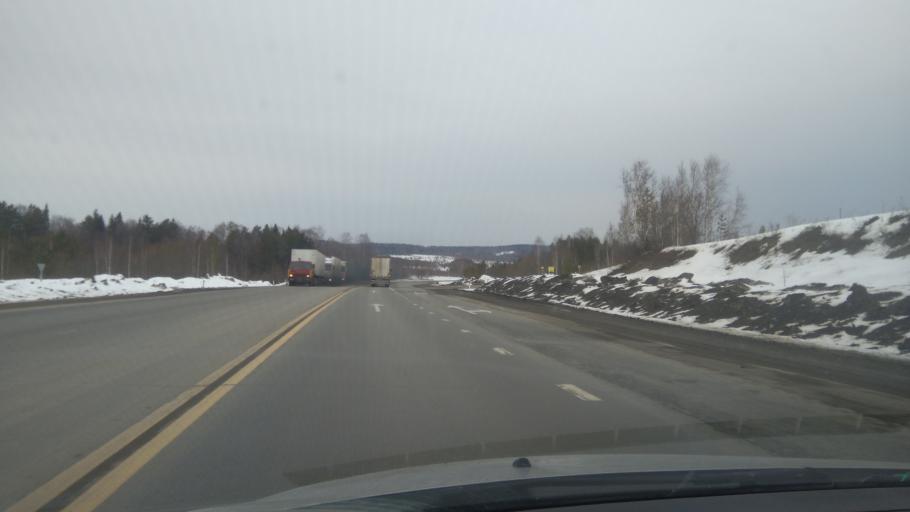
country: RU
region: Sverdlovsk
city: Ufimskiy
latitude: 56.7868
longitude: 58.3651
